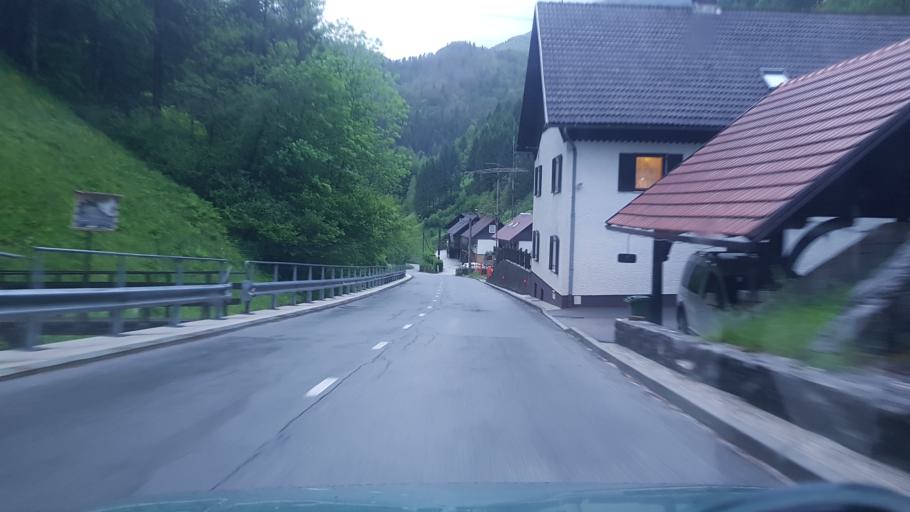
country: SI
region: Bohinj
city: Bohinjska Bistrica
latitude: 46.2148
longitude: 13.9812
